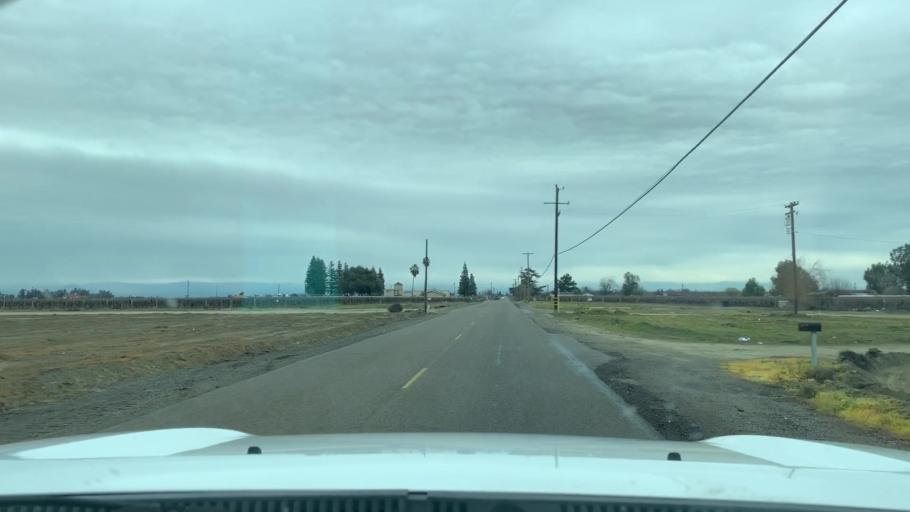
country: US
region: California
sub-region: Fresno County
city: Fowler
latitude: 36.5473
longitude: -119.7329
